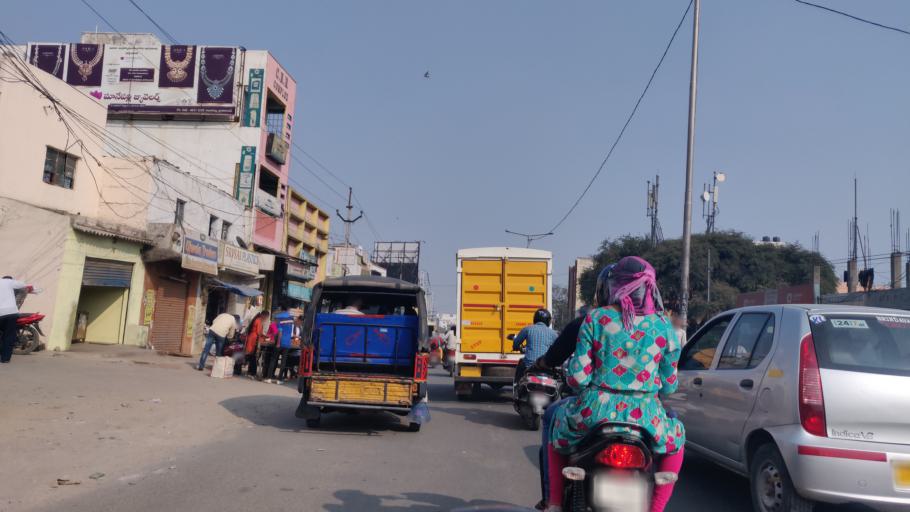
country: IN
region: Telangana
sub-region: Rangareddi
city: Uppal Kalan
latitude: 17.4015
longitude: 78.5697
